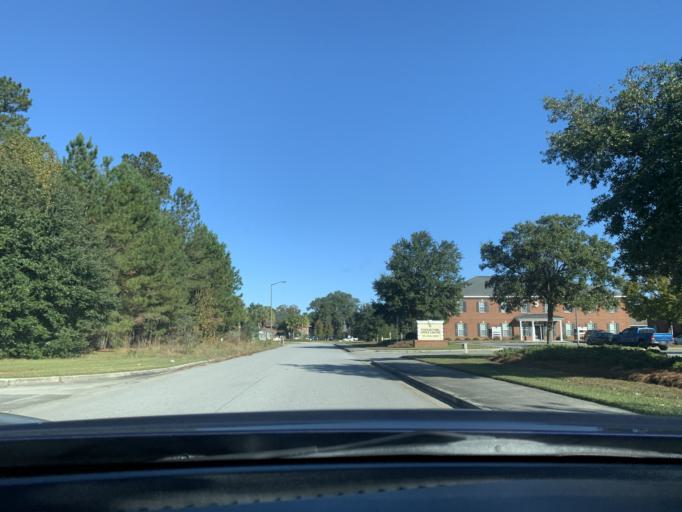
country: US
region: Georgia
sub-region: Chatham County
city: Pooler
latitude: 32.1299
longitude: -81.2553
